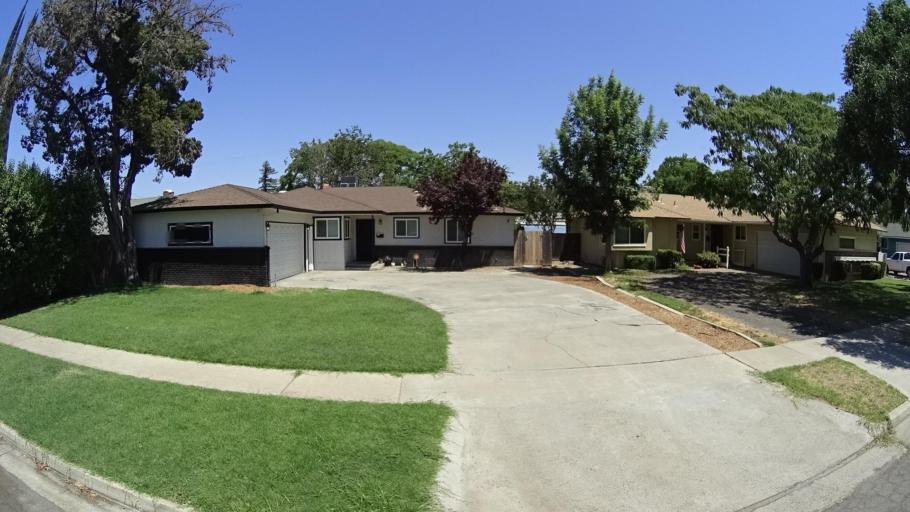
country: US
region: California
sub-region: Fresno County
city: Fresno
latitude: 36.7859
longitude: -119.7761
